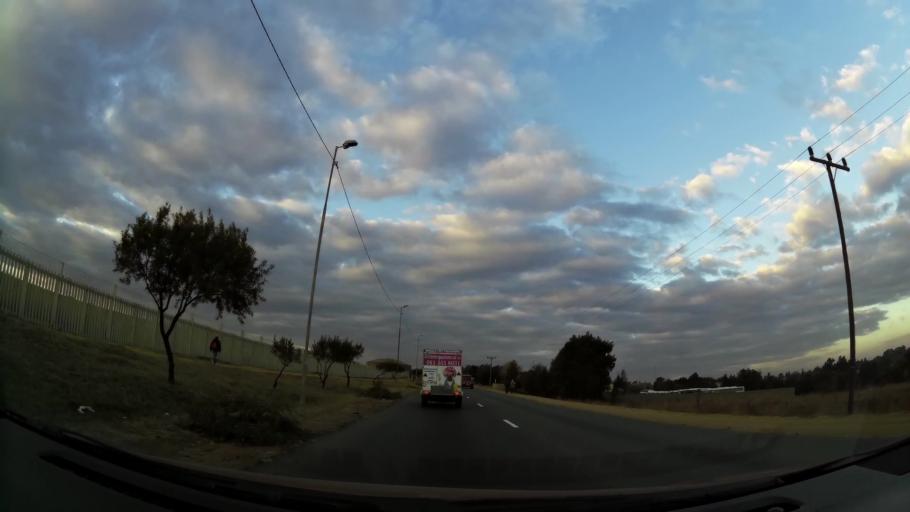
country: ZA
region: Gauteng
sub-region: City of Johannesburg Metropolitan Municipality
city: Midrand
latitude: -25.9969
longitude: 28.1432
